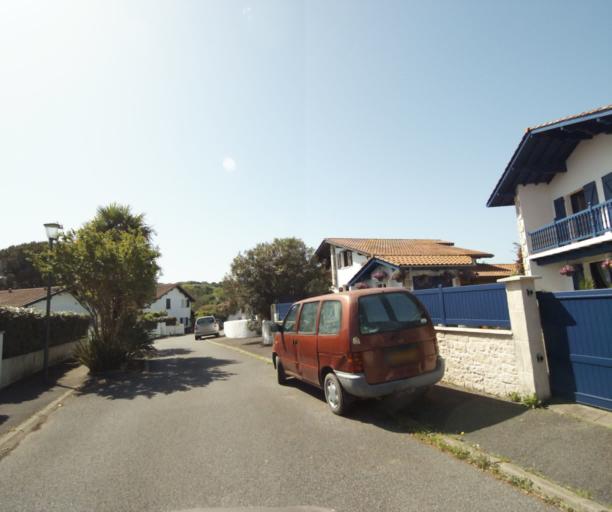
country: FR
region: Aquitaine
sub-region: Departement des Pyrenees-Atlantiques
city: Mouguerre
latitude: 43.4640
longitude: -1.4451
